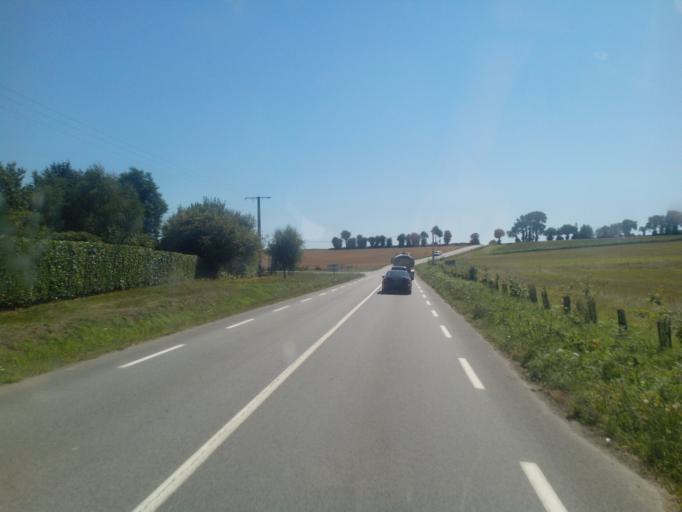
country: FR
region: Brittany
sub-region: Departement du Morbihan
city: Guillac
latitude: 47.8619
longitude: -2.4250
